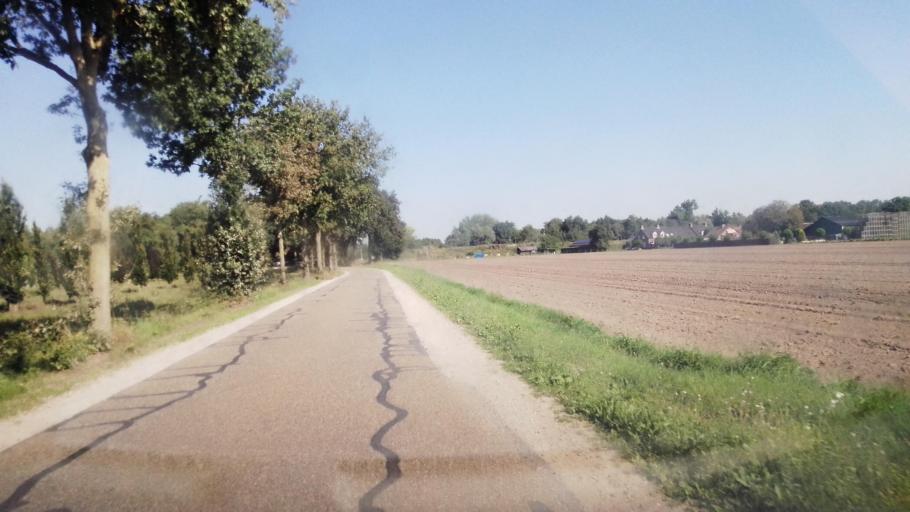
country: NL
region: Limburg
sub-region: Gemeente Peel en Maas
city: Maasbree
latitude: 51.3761
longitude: 6.0070
